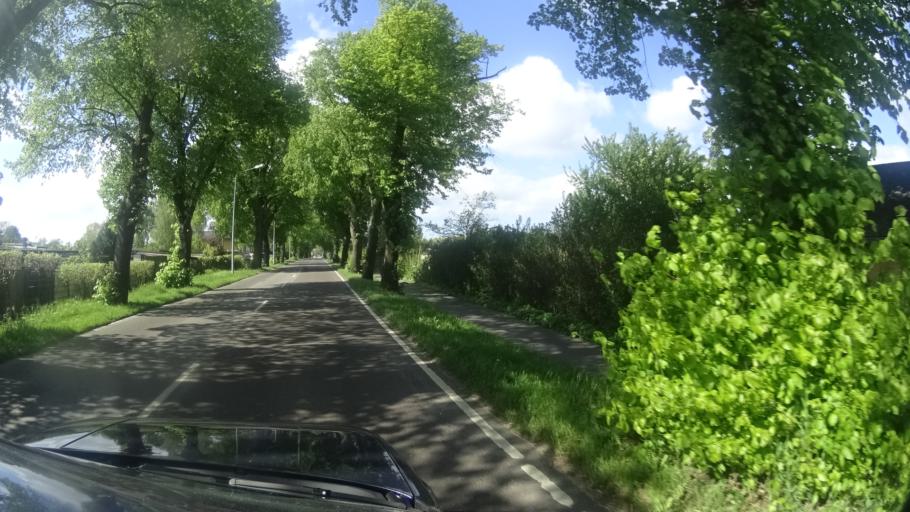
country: DE
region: Mecklenburg-Vorpommern
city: Dierkow-Neu
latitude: 54.0857
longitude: 12.1643
